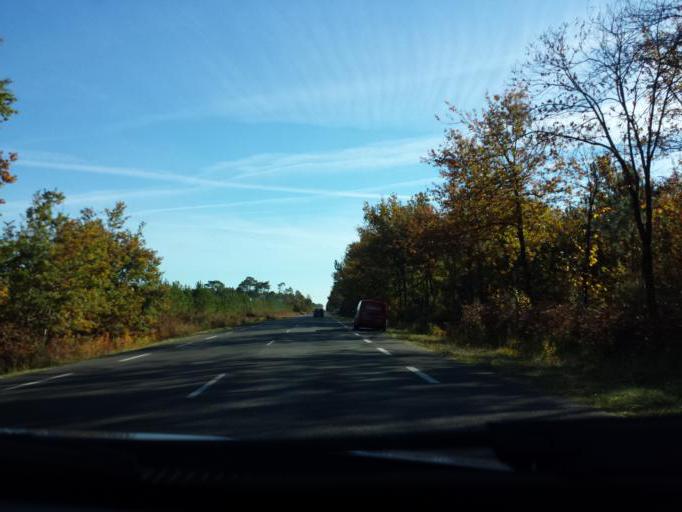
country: FR
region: Aquitaine
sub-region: Departement de la Gironde
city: Sainte-Helene
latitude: 44.9733
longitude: -0.9786
